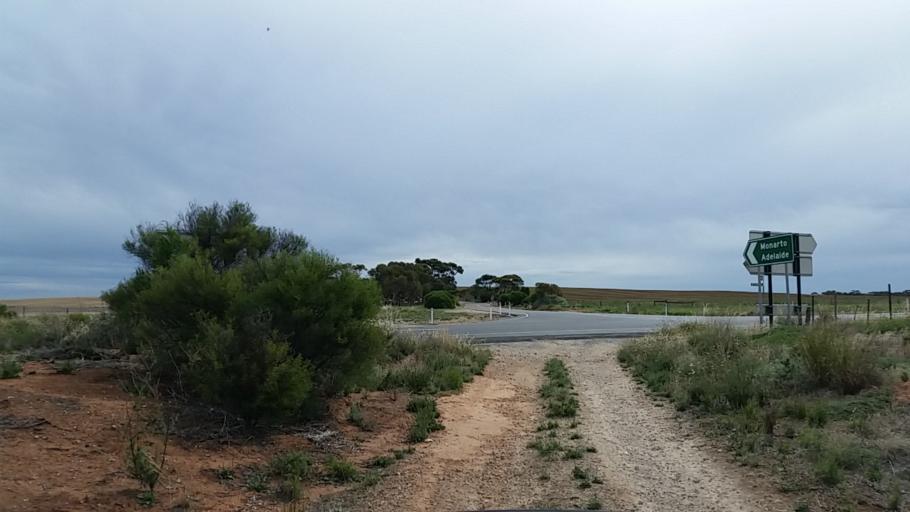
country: AU
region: South Australia
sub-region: Murray Bridge
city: Murray Bridge
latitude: -35.0342
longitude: 139.2046
